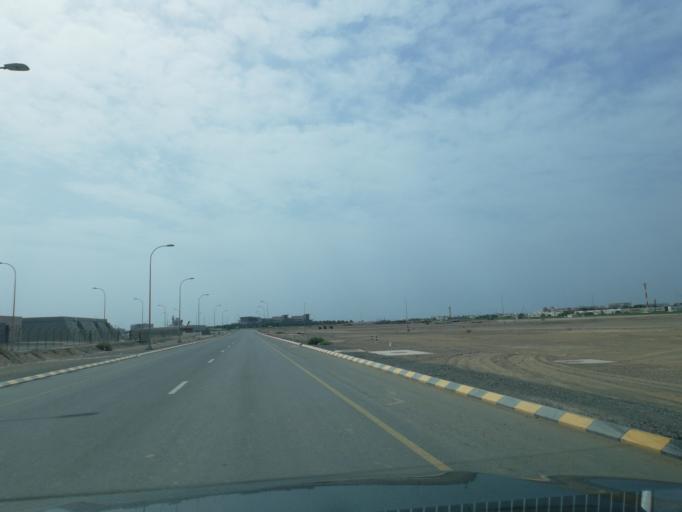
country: OM
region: Muhafazat Masqat
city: As Sib al Jadidah
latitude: 23.6163
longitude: 58.2746
